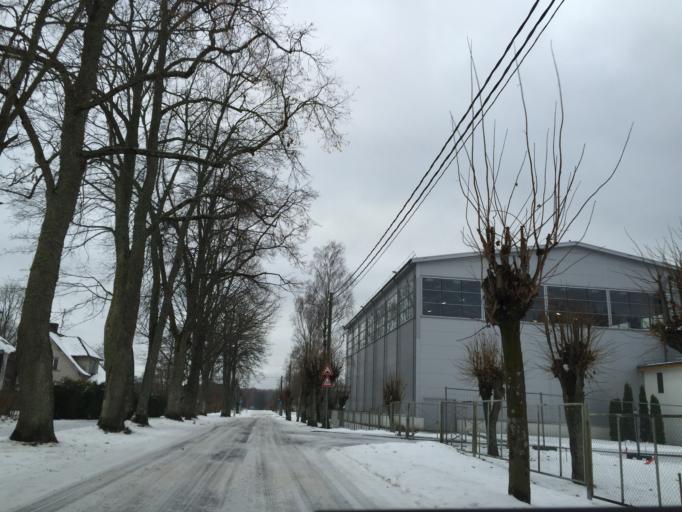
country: LV
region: Saulkrastu
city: Saulkrasti
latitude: 57.2620
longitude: 24.4185
